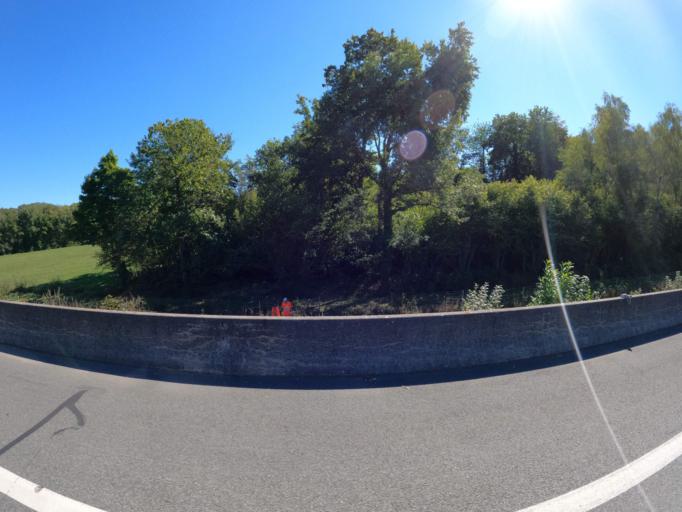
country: FR
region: Limousin
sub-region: Departement de la Creuse
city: Ajain
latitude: 46.2053
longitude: 2.0064
